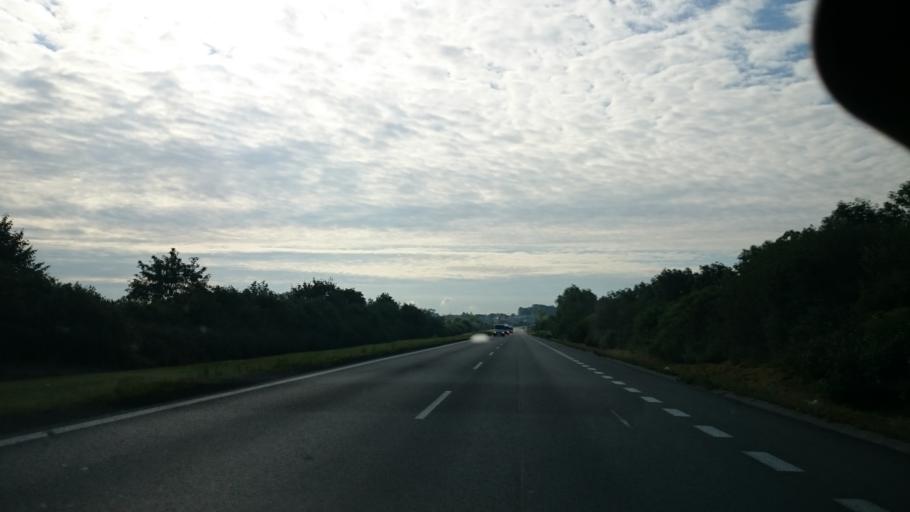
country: PL
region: Opole Voivodeship
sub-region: Powiat opolski
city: Opole
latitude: 50.7006
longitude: 17.9482
